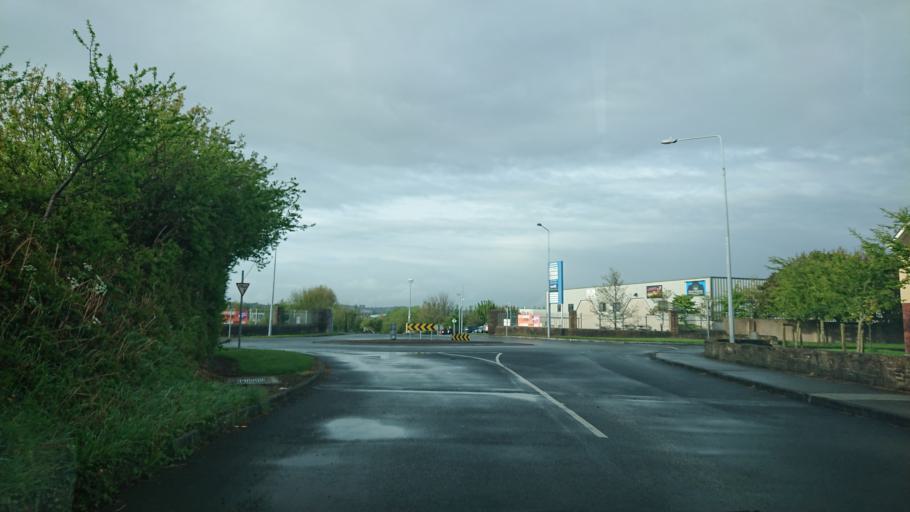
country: IE
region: Munster
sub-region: Waterford
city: Waterford
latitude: 52.2413
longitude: -7.1306
